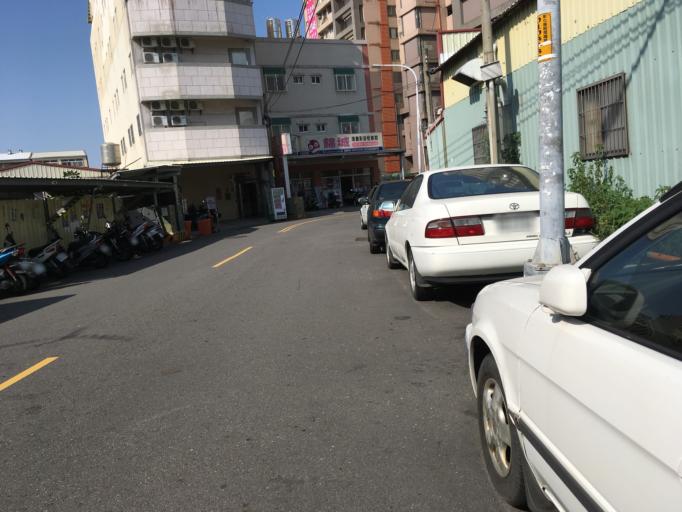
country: TW
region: Taiwan
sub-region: Changhua
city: Chang-hua
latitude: 24.0846
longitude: 120.5571
